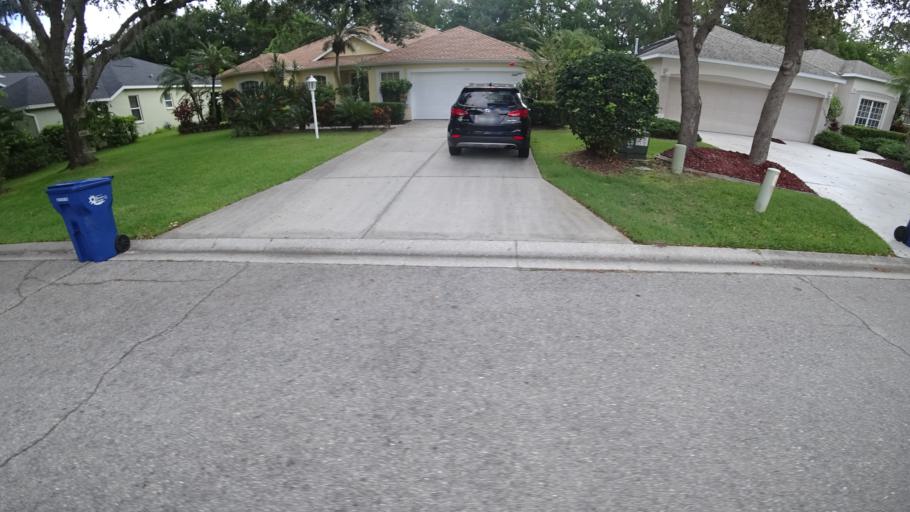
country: US
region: Florida
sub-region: Sarasota County
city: The Meadows
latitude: 27.4206
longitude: -82.4306
